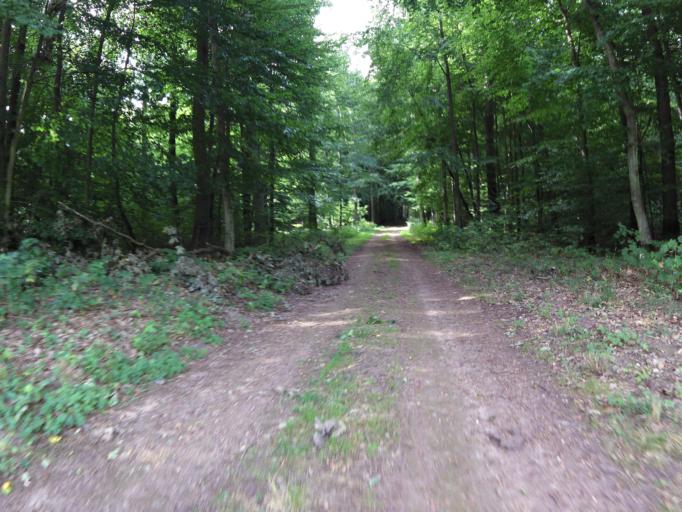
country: DE
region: Mecklenburg-Vorpommern
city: Seebad Bansin
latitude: 53.9484
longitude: 14.1022
